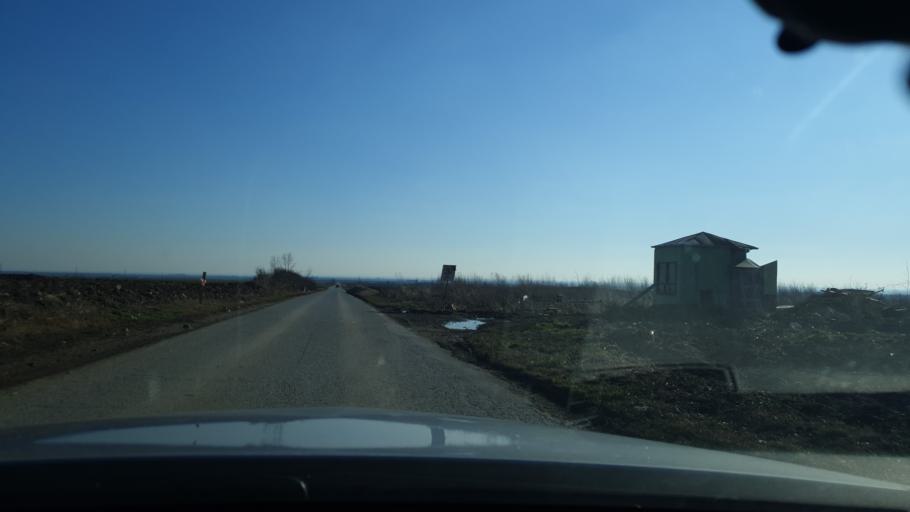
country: RS
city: Vrdnik
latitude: 45.0886
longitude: 19.8064
